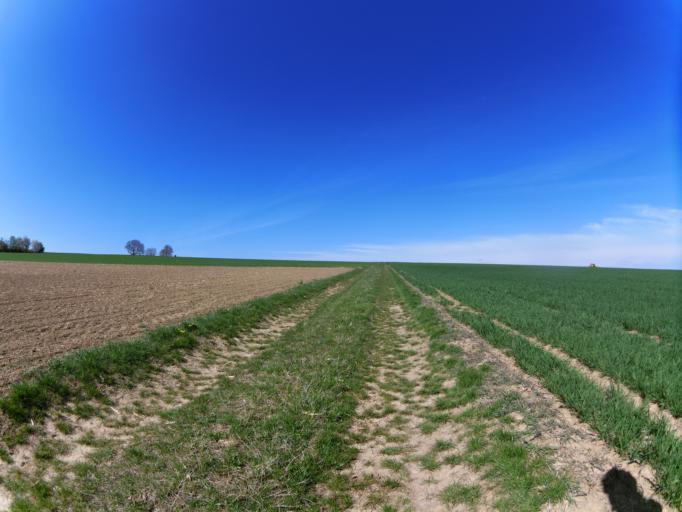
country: DE
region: Bavaria
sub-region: Regierungsbezirk Unterfranken
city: Winterhausen
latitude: 49.6823
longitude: 10.0009
